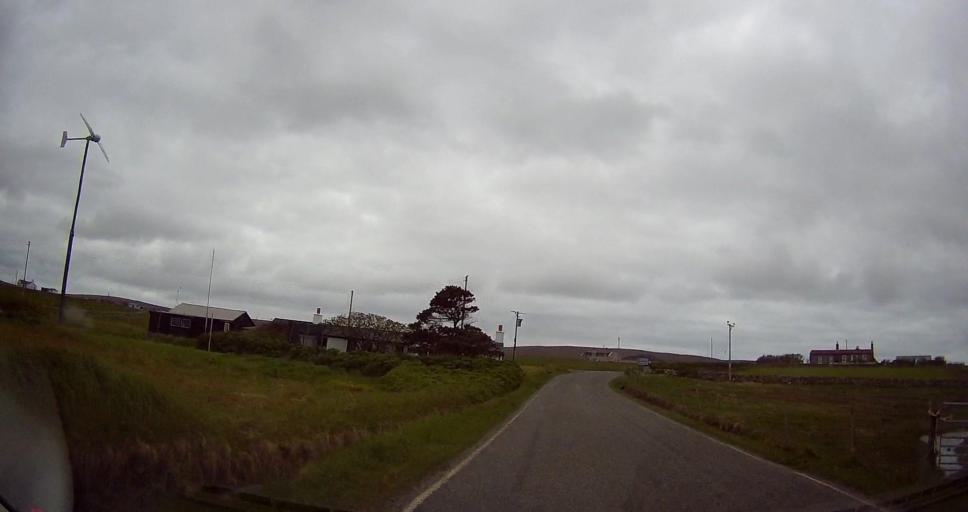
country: GB
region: Scotland
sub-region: Shetland Islands
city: Shetland
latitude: 60.7577
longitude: -0.8660
